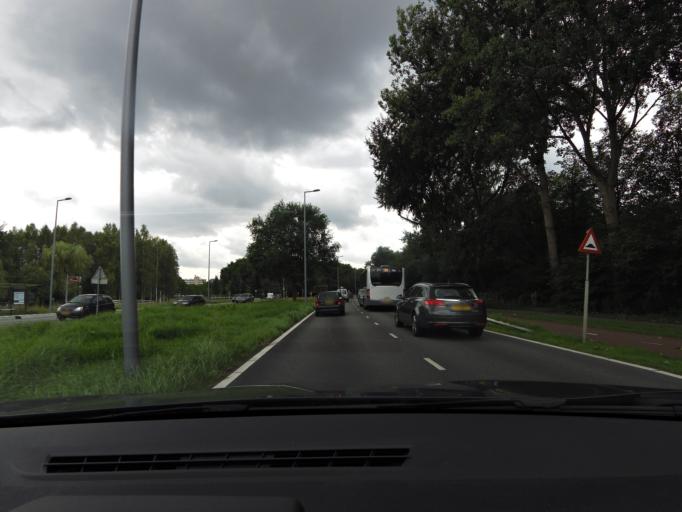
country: NL
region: South Holland
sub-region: Gemeente Rotterdam
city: Delfshaven
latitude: 51.8829
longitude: 4.4708
